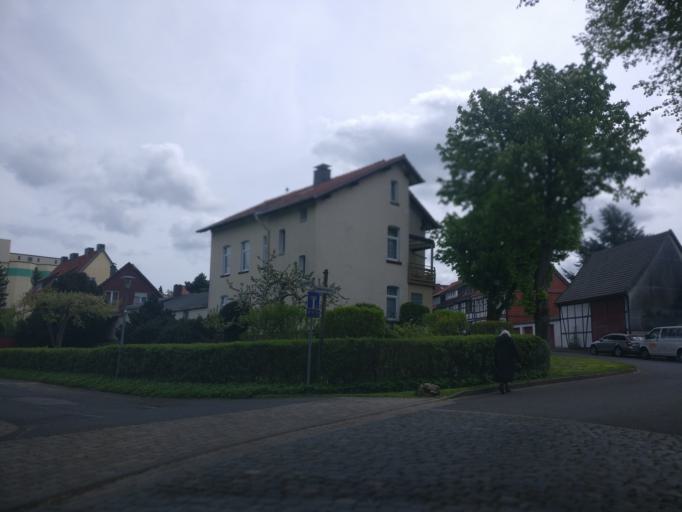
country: DE
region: Lower Saxony
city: Dransfeld
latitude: 51.5045
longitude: 9.7600
